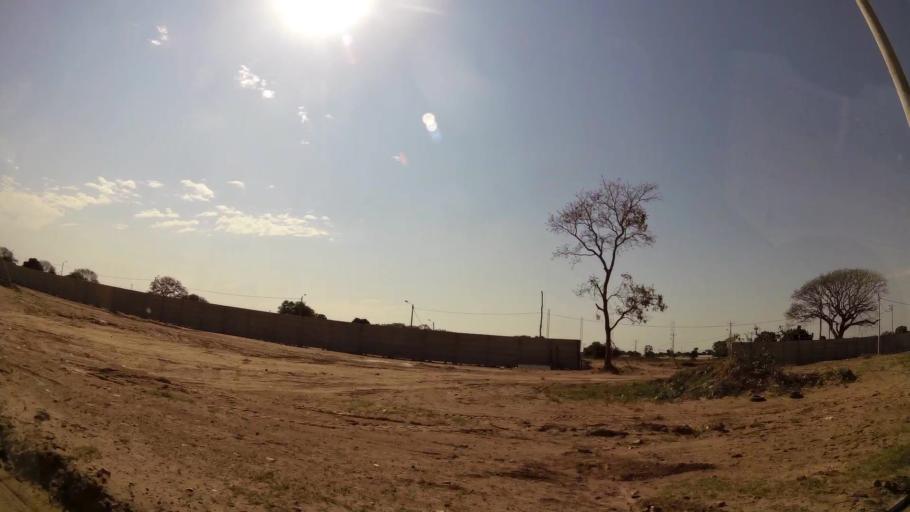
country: BO
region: Santa Cruz
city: Cotoca
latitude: -17.7549
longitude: -63.1016
